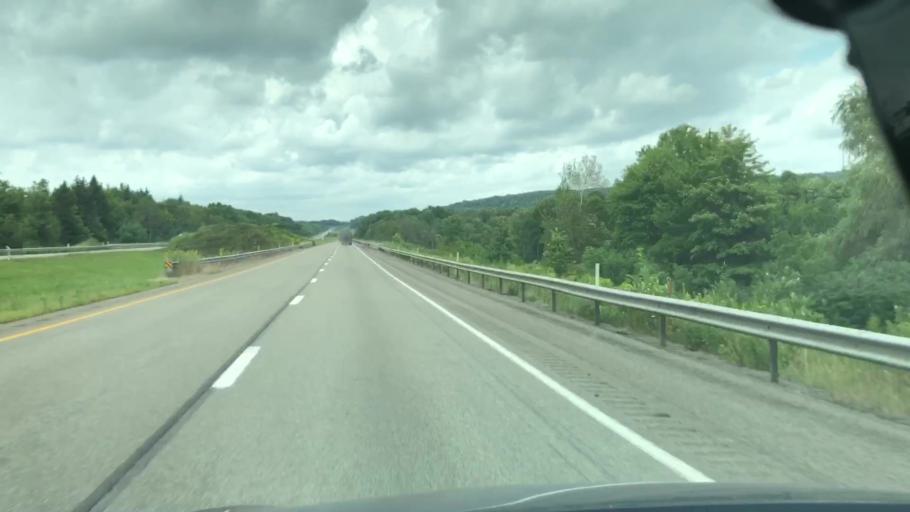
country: US
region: Pennsylvania
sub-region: Crawford County
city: Meadville
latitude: 41.6511
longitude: -80.2044
